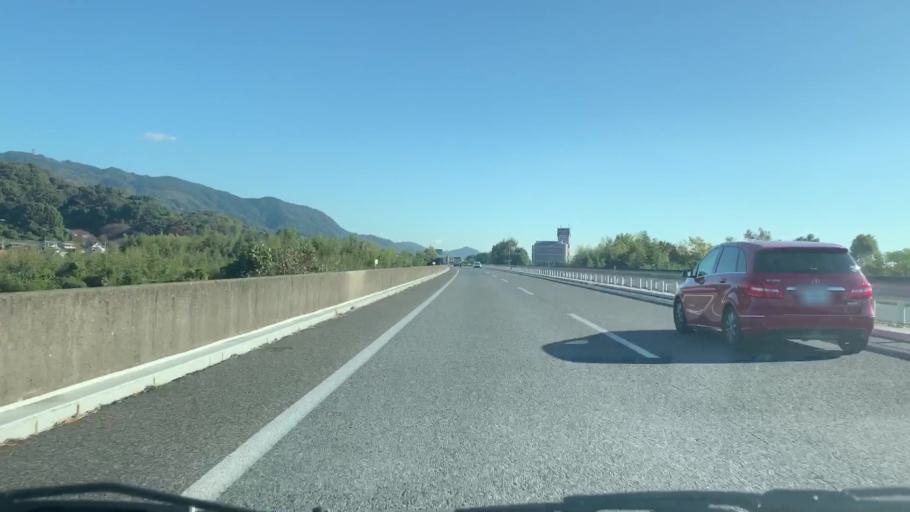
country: JP
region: Saga Prefecture
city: Saga-shi
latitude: 33.3184
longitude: 130.2687
